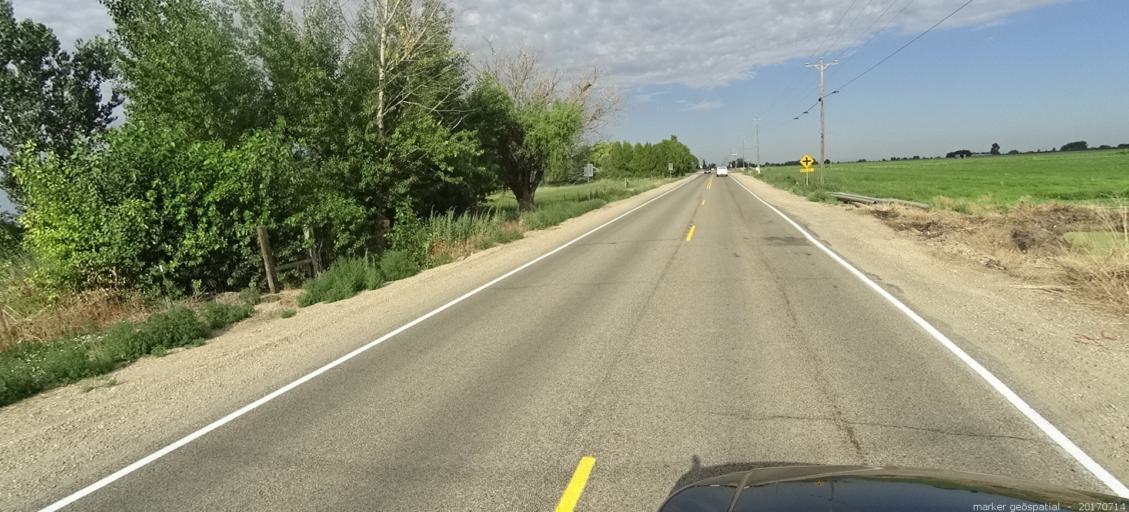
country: US
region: Idaho
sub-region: Ada County
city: Kuna
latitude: 43.4884
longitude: -116.4513
